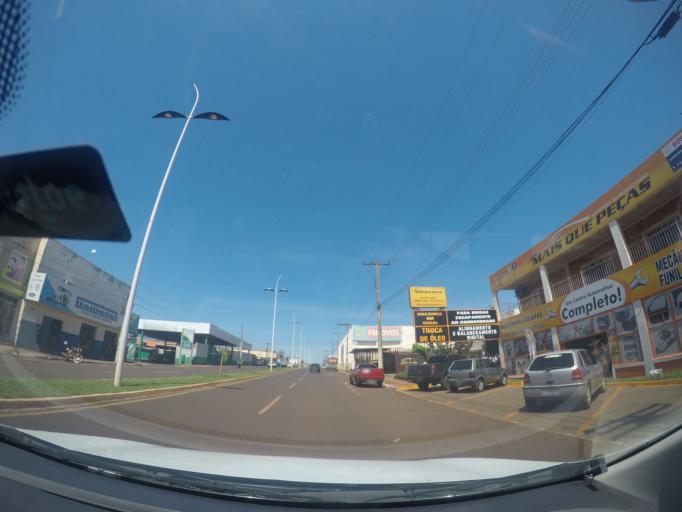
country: BR
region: Goias
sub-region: Itumbiara
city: Itumbiara
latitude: -18.4026
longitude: -49.2065
